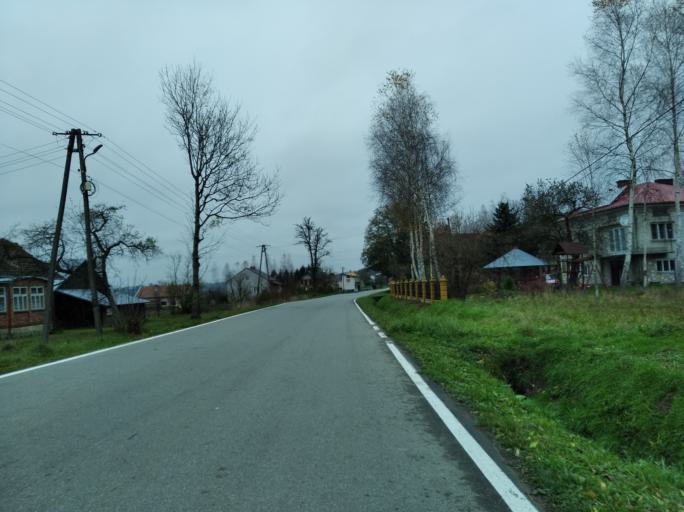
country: PL
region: Subcarpathian Voivodeship
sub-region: Powiat krosnienski
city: Leki
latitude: 49.8218
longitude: 21.6451
